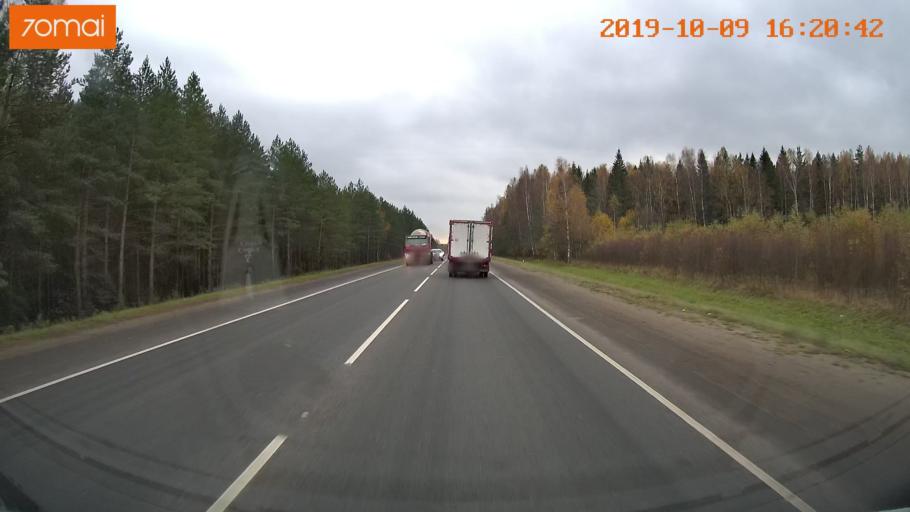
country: RU
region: Kostroma
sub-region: Kostromskoy Rayon
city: Kostroma
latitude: 57.7030
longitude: 40.8914
